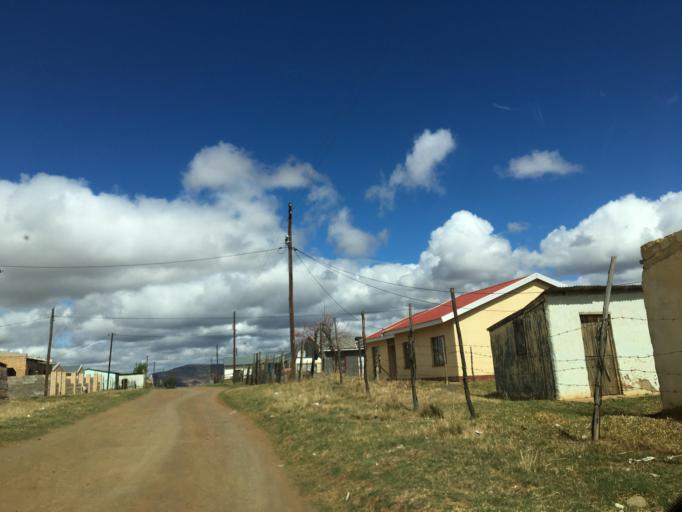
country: ZA
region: Eastern Cape
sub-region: Chris Hani District Municipality
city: Cala
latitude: -31.5296
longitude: 27.7045
